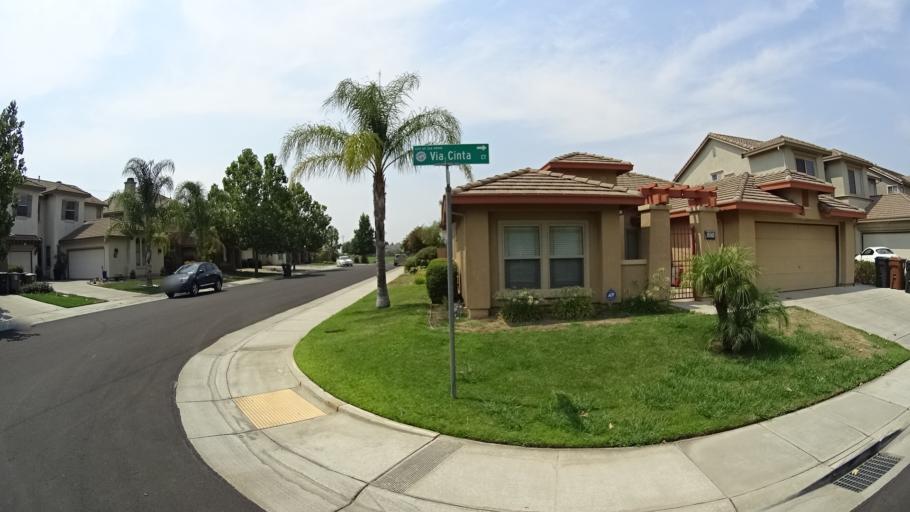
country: US
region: California
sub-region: Sacramento County
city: Laguna
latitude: 38.3800
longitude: -121.4282
